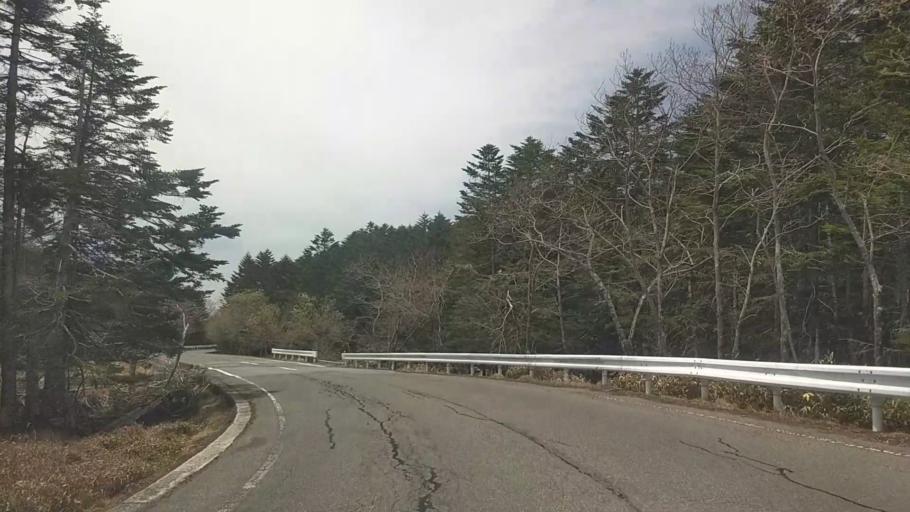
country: JP
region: Nagano
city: Chino
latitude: 36.0551
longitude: 138.3344
